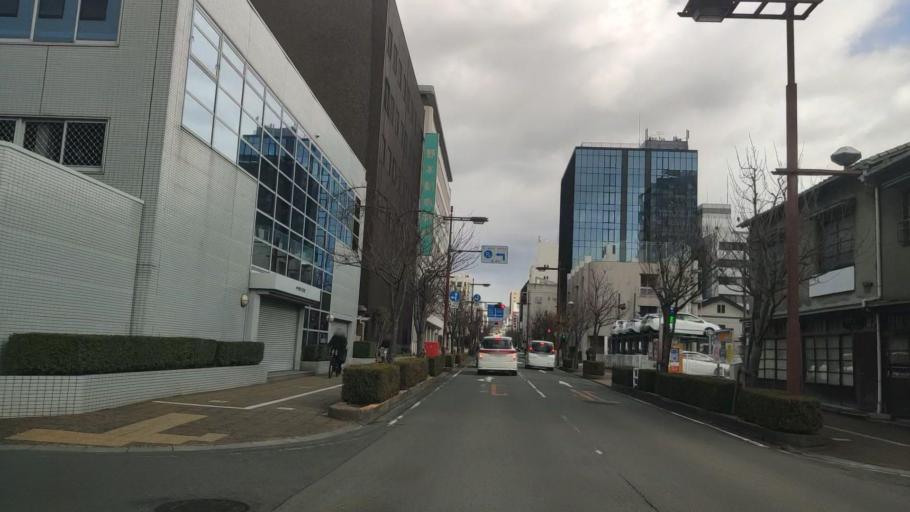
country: JP
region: Ehime
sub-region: Shikoku-chuo Shi
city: Matsuyama
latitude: 33.8384
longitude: 132.7633
